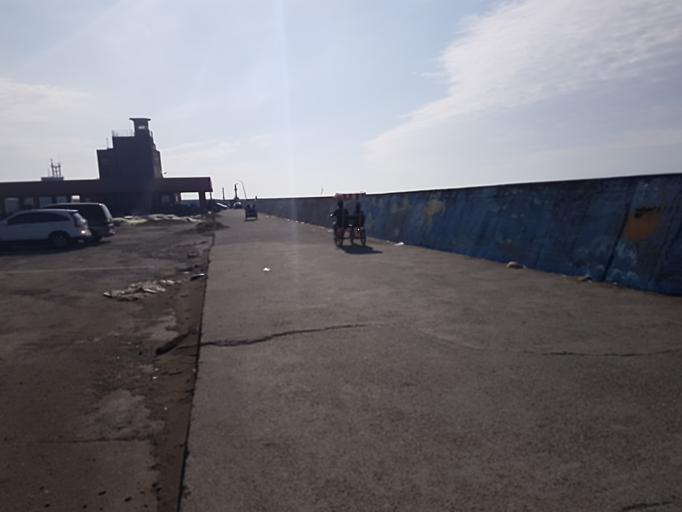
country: TW
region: Taiwan
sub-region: Hsinchu
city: Hsinchu
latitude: 24.8498
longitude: 120.9210
